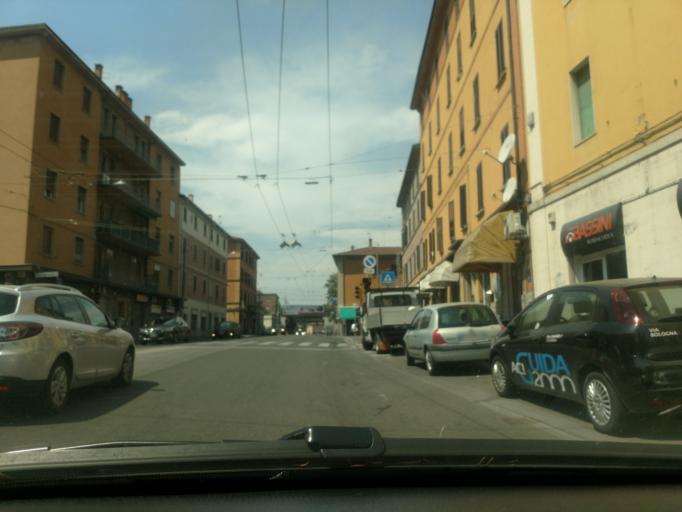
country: IT
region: Emilia-Romagna
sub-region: Provincia di Bologna
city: Bologna
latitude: 44.4932
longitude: 11.3773
